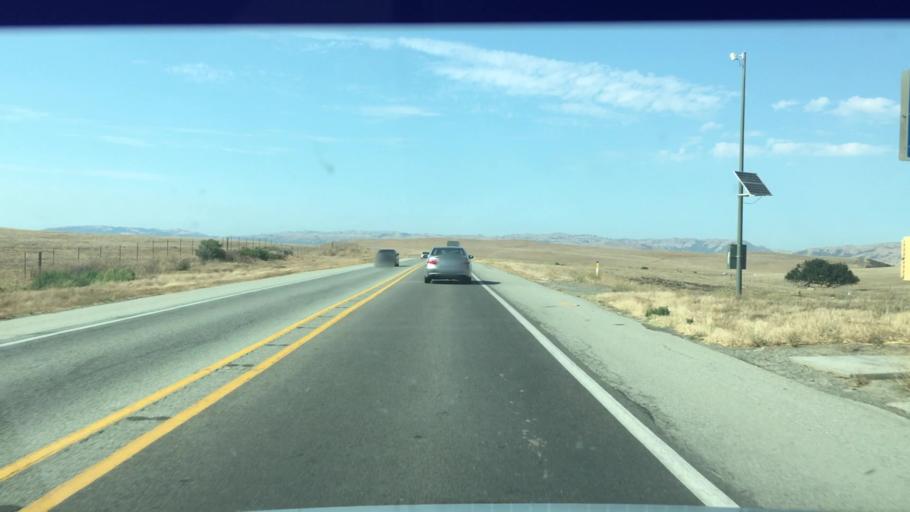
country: US
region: California
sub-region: San Benito County
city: Hollister
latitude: 36.8688
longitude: -121.4422
